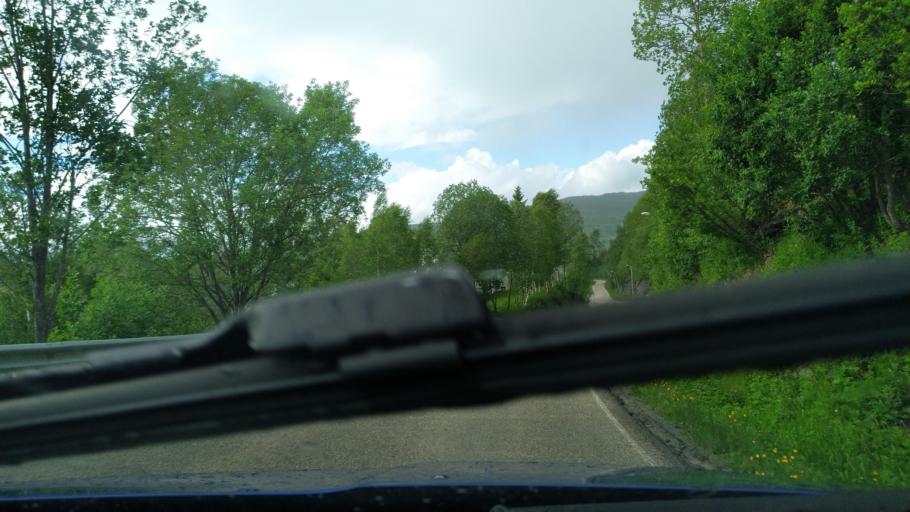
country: NO
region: Troms
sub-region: Sorreisa
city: Sorreisa
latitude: 69.1623
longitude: 18.1169
